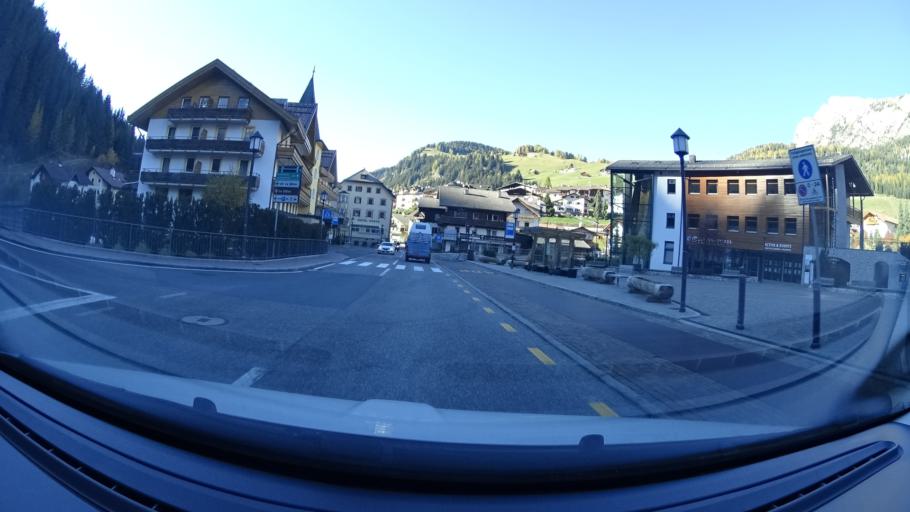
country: IT
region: Trentino-Alto Adige
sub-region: Bolzano
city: Selva
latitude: 46.5555
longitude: 11.7566
